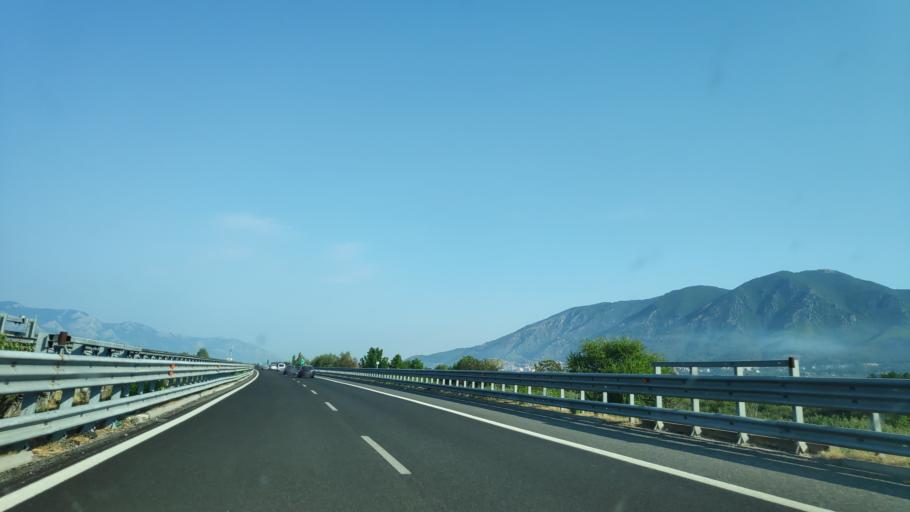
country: IT
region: Campania
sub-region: Provincia di Salerno
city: Sala Consilina
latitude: 40.3611
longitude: 15.6092
